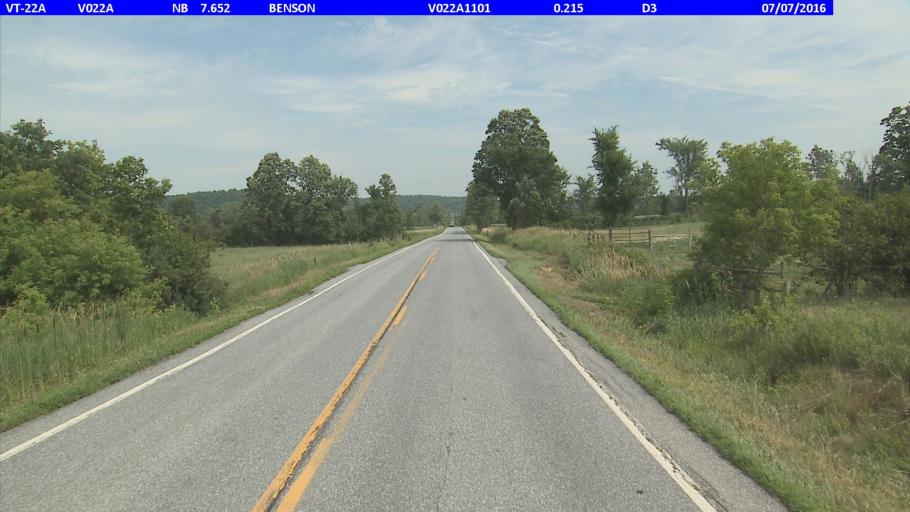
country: US
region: Vermont
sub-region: Rutland County
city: Fair Haven
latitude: 43.6724
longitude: -73.2891
